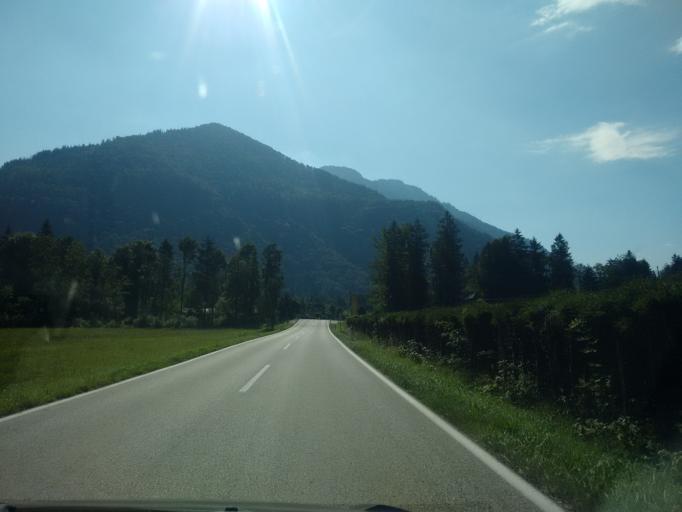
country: AT
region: Upper Austria
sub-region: Politischer Bezirk Gmunden
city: Gruenau im Almtal
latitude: 47.8359
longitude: 13.9498
